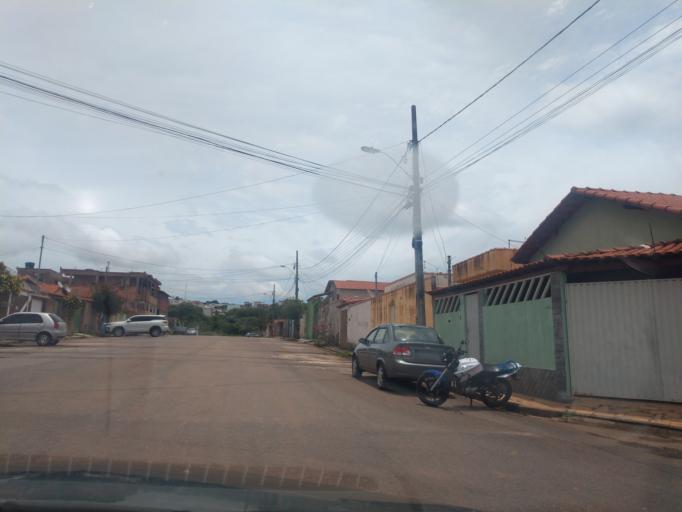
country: BR
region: Minas Gerais
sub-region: Tres Coracoes
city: Tres Coracoes
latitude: -21.6791
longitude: -45.2599
